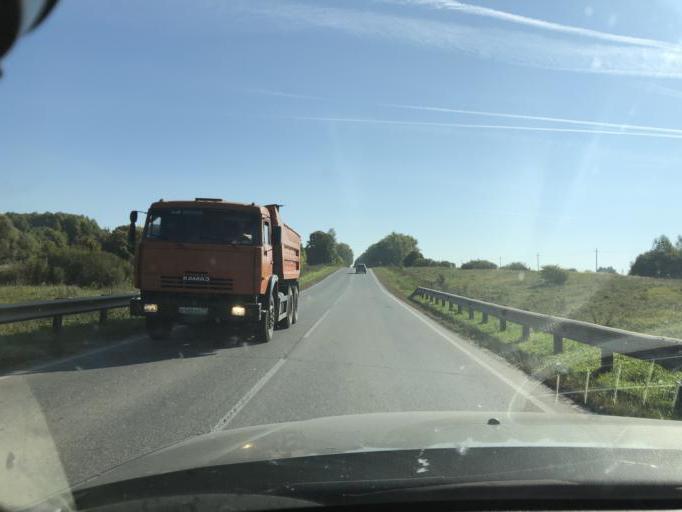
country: RU
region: Tula
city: Yasnogorsk
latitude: 54.4686
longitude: 37.6323
